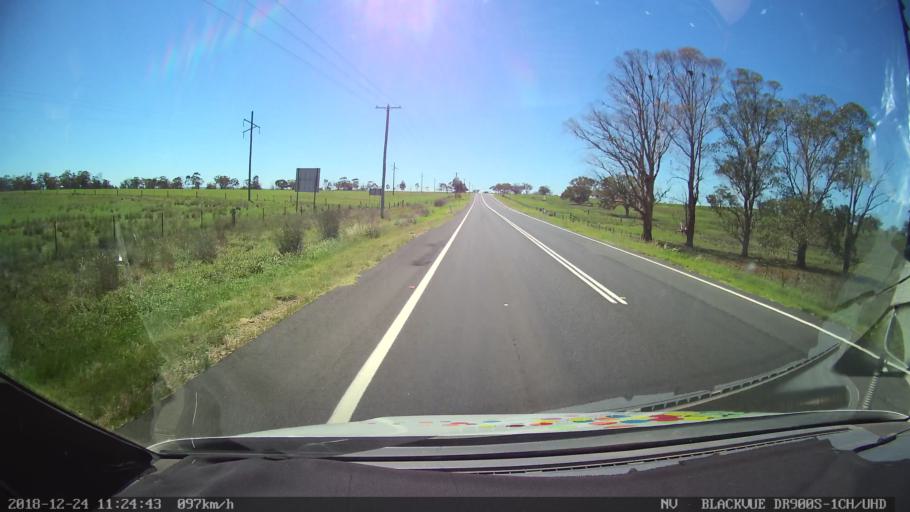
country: AU
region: New South Wales
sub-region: Upper Hunter Shire
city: Merriwa
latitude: -32.1658
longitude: 150.4052
